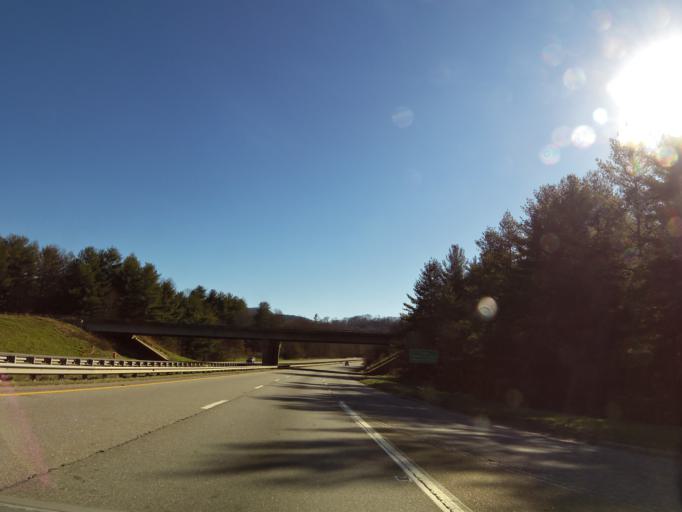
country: US
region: North Carolina
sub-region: Haywood County
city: Lake Junaluska
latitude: 35.5704
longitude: -82.9586
